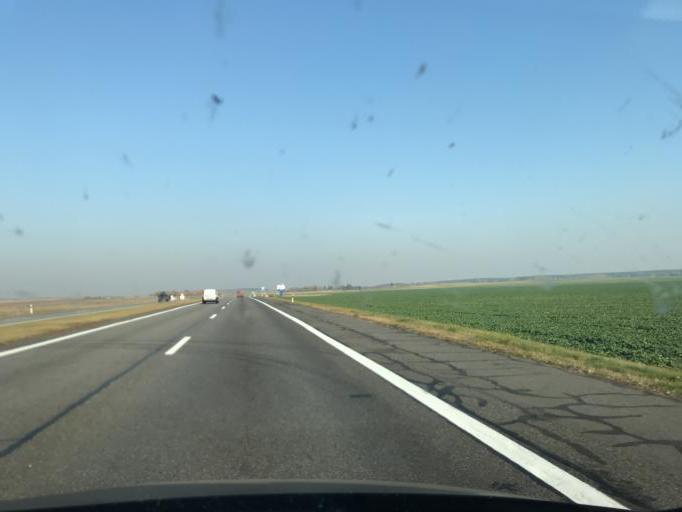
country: BY
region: Minsk
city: Snow
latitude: 53.2729
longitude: 26.3039
